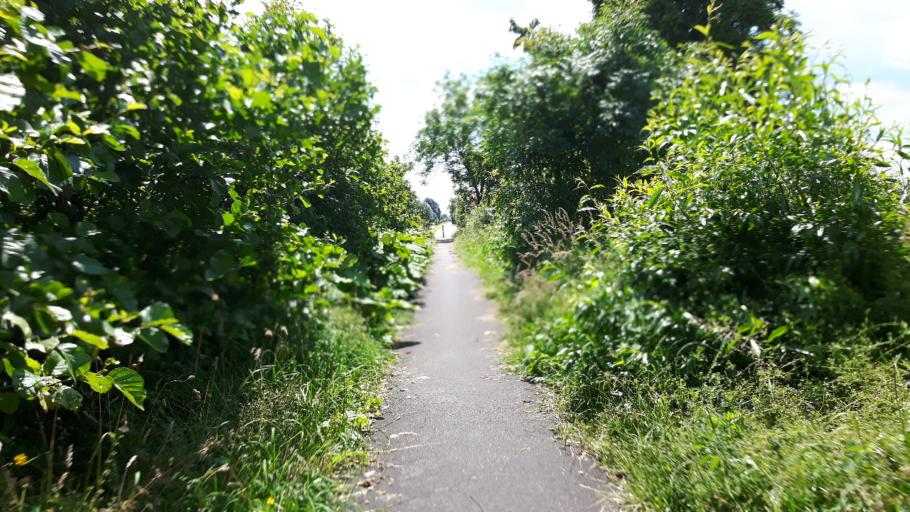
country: NL
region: South Holland
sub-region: Gemeente Boskoop
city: Boskoop
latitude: 52.0775
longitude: 4.6880
